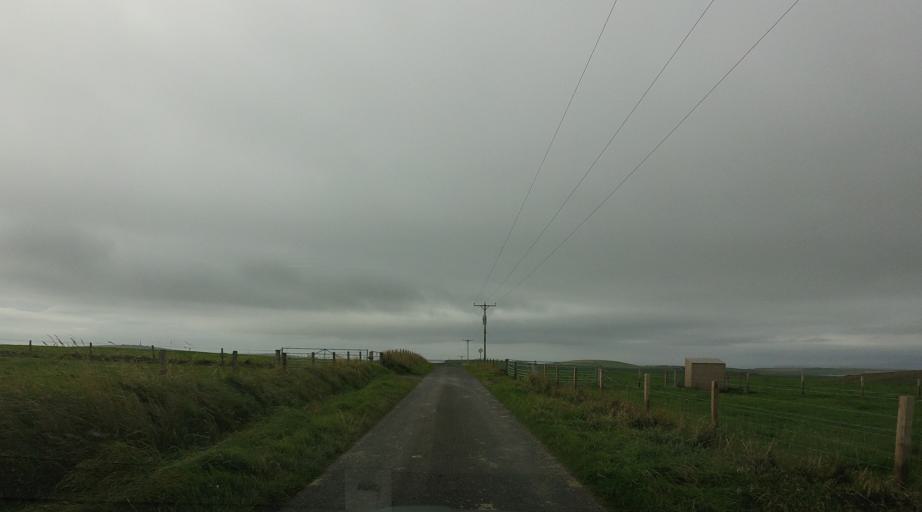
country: GB
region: Scotland
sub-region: Orkney Islands
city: Orkney
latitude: 58.8084
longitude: -2.9324
